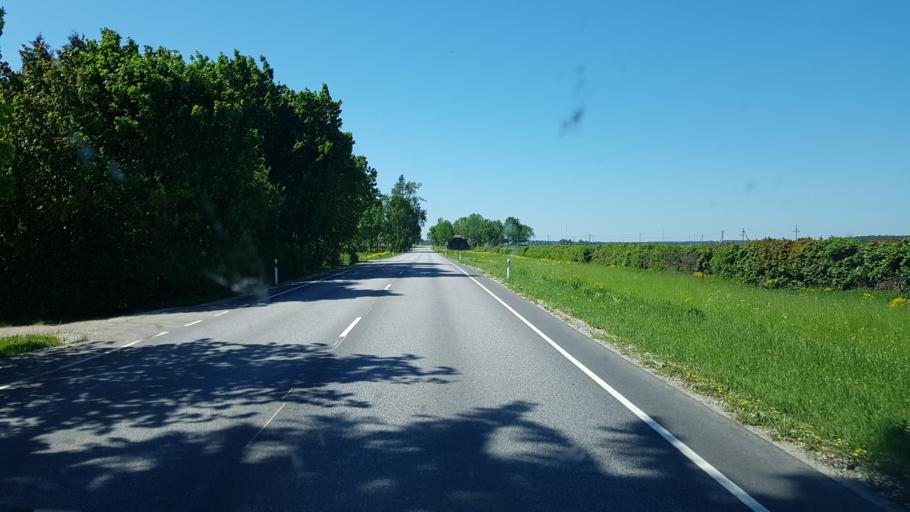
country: EE
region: Laeaene-Virumaa
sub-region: Vinni vald
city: Vinni
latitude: 59.2317
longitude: 26.5102
